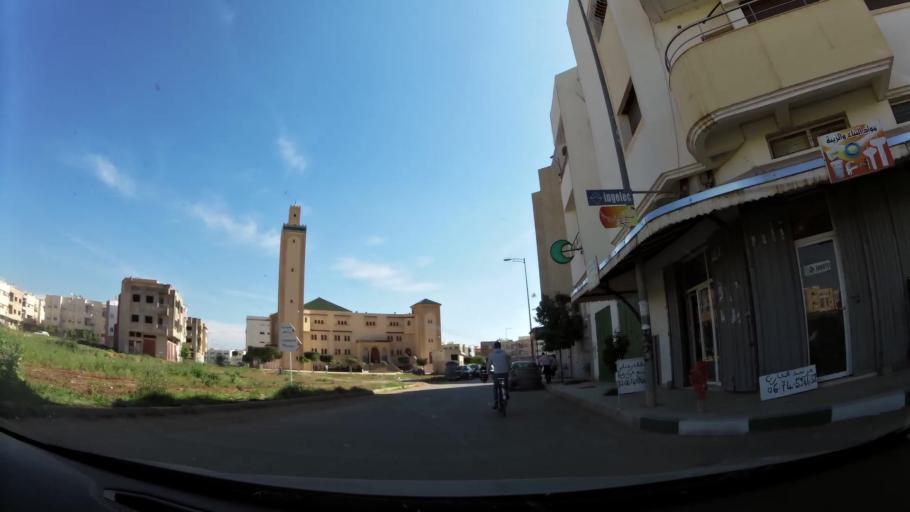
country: MA
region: Fes-Boulemane
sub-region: Fes
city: Fes
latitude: 33.9993
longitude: -5.0091
